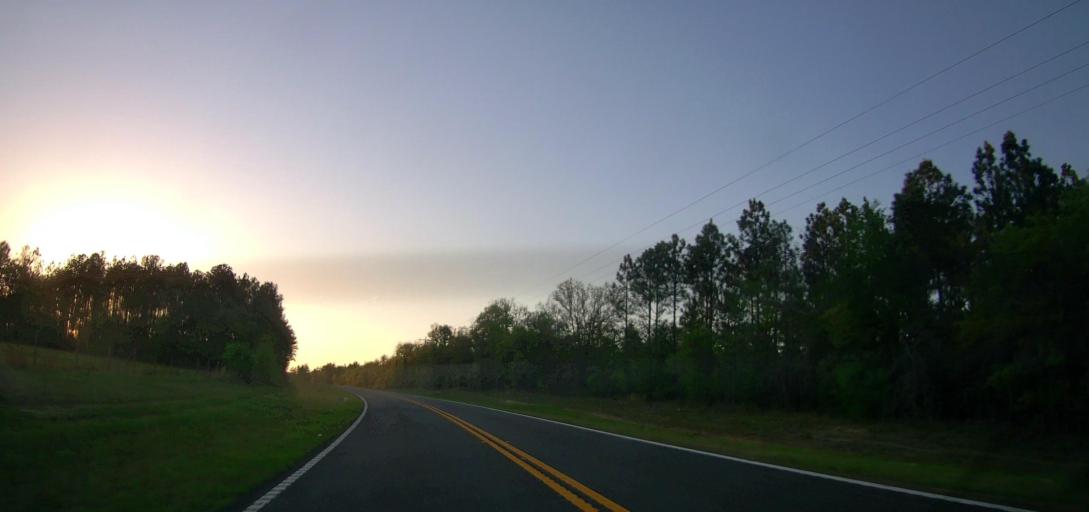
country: US
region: Georgia
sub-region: Marion County
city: Buena Vista
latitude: 32.4397
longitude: -84.6014
